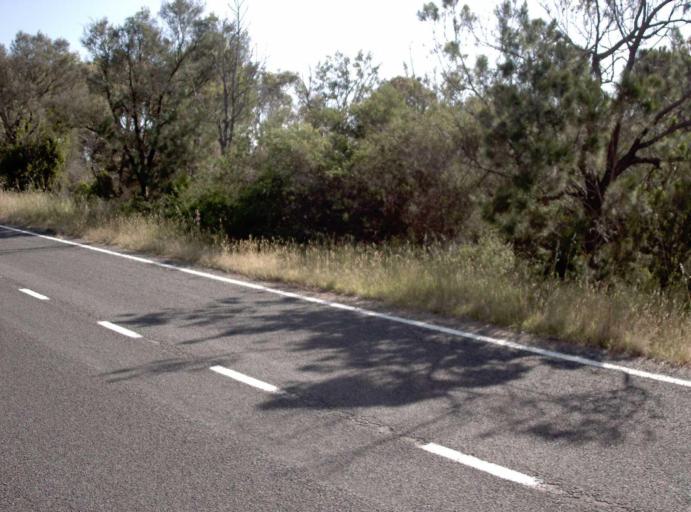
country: AU
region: Victoria
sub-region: Cardinia
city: Koo-Wee-Rup
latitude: -38.3084
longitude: 145.5420
